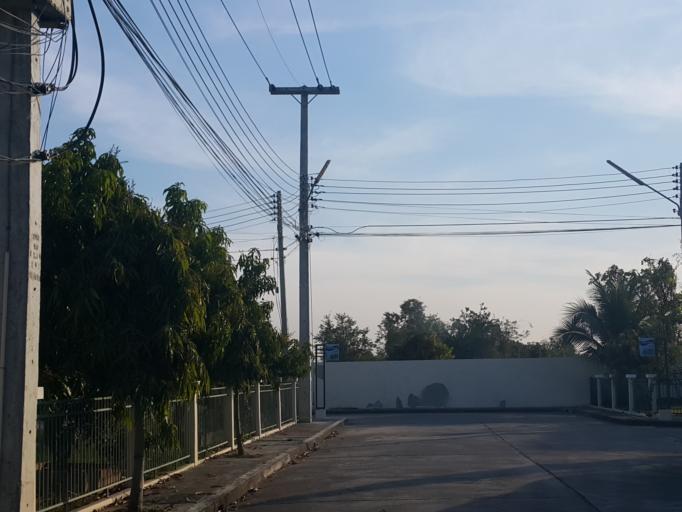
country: TH
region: Chiang Mai
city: San Sai
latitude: 18.8108
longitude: 99.0766
